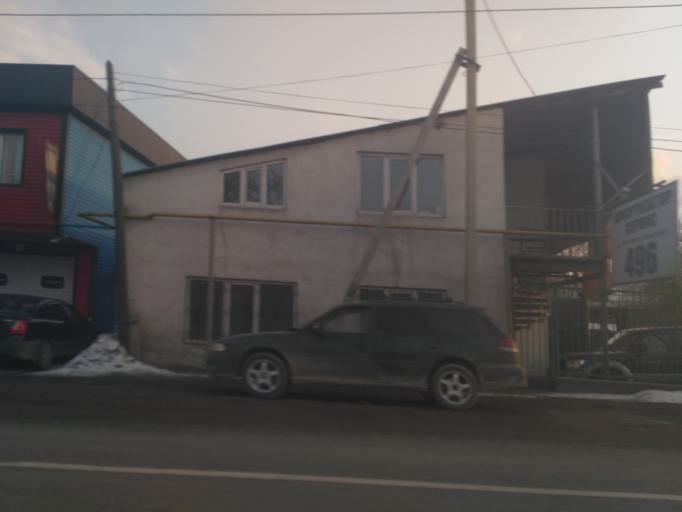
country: KZ
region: Almaty Qalasy
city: Almaty
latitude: 43.2487
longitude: 76.8445
